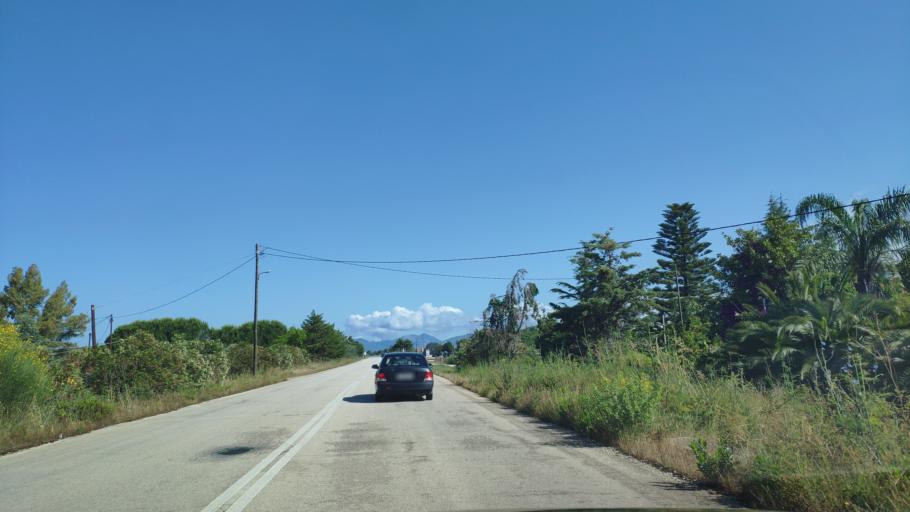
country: GR
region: Epirus
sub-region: Nomos Prevezis
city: Preveza
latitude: 38.9685
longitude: 20.7238
